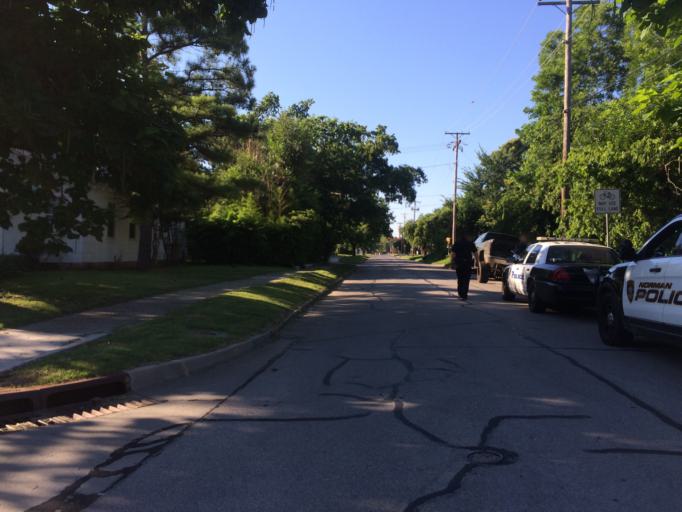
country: US
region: Oklahoma
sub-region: Cleveland County
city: Norman
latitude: 35.2218
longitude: -97.4499
